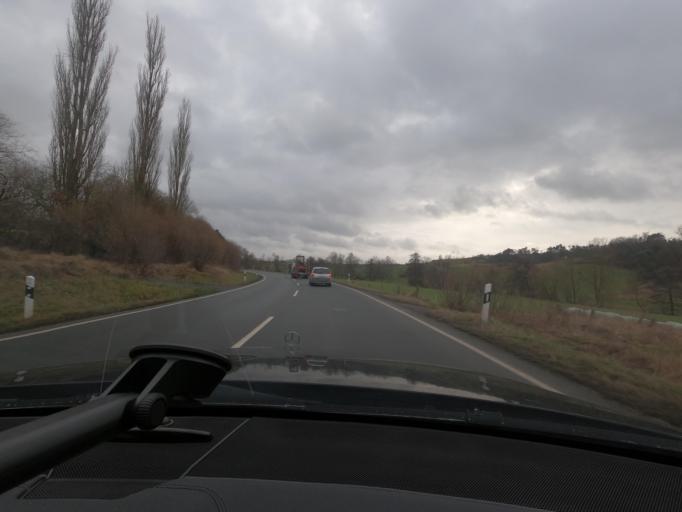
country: DE
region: Hesse
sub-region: Regierungsbezirk Kassel
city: Volkmarsen
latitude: 51.3935
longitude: 9.1391
